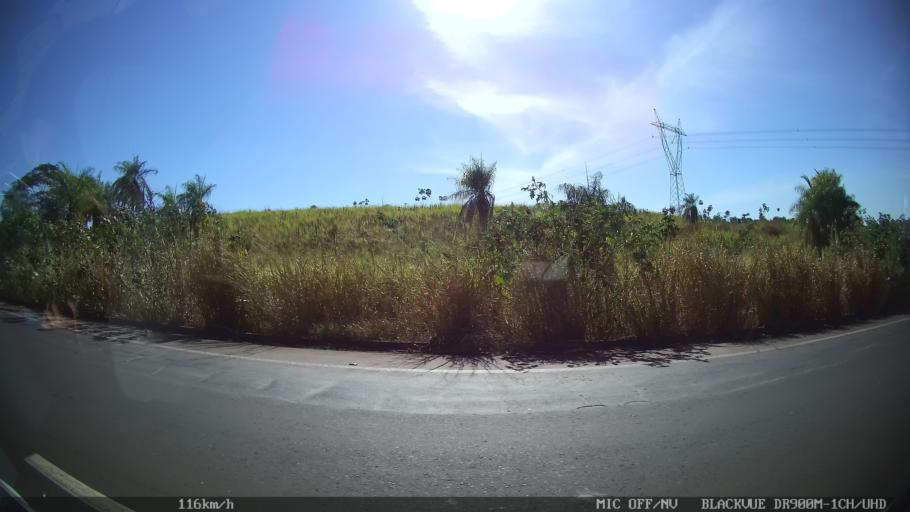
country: BR
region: Sao Paulo
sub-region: Olimpia
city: Olimpia
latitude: -20.6329
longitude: -48.8146
